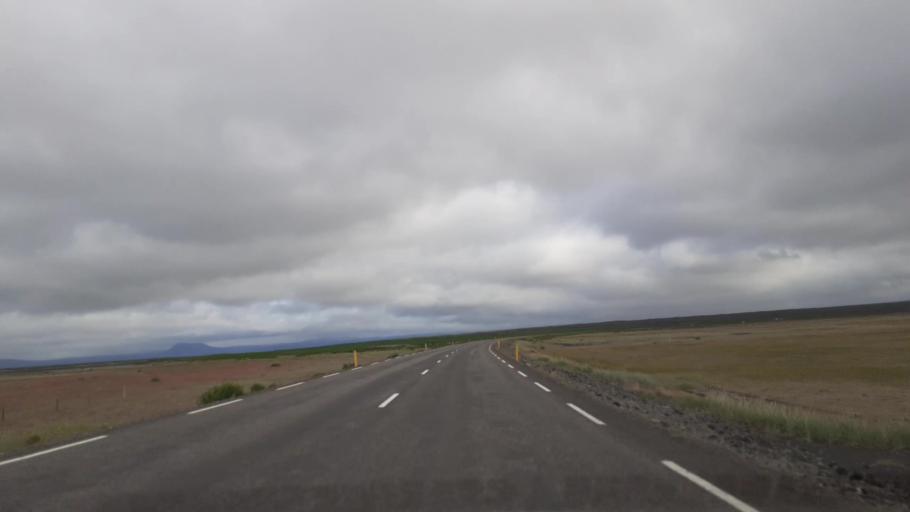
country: IS
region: Northeast
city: Husavik
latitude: 66.1183
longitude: -16.9187
